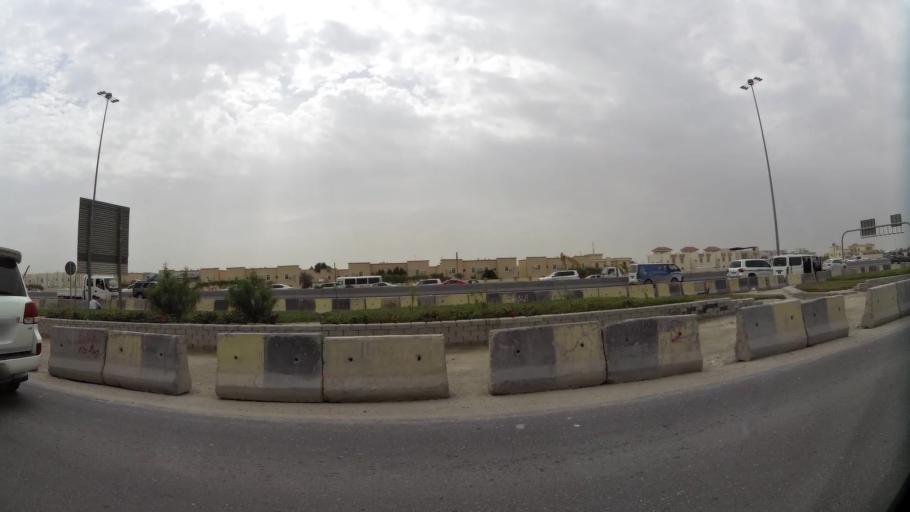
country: QA
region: Baladiyat ar Rayyan
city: Ar Rayyan
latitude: 25.3497
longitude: 51.4559
